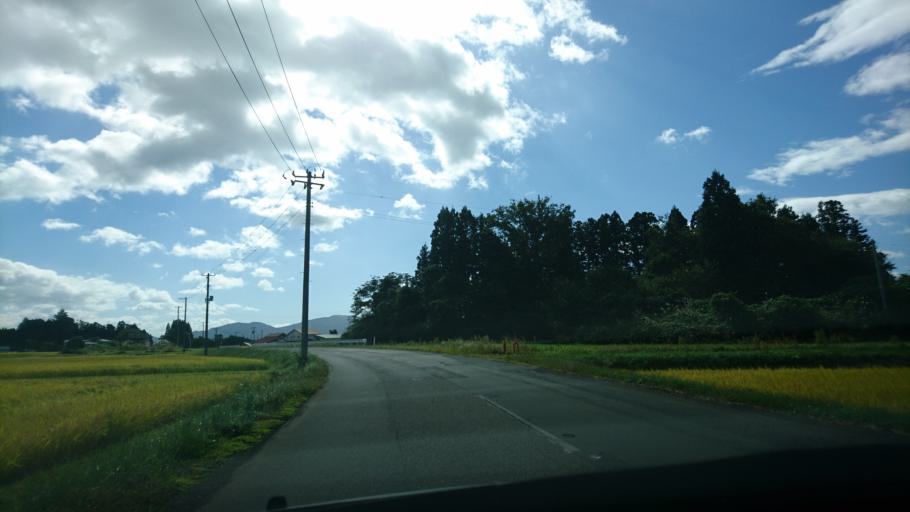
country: JP
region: Iwate
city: Mizusawa
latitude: 39.0793
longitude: 141.1045
